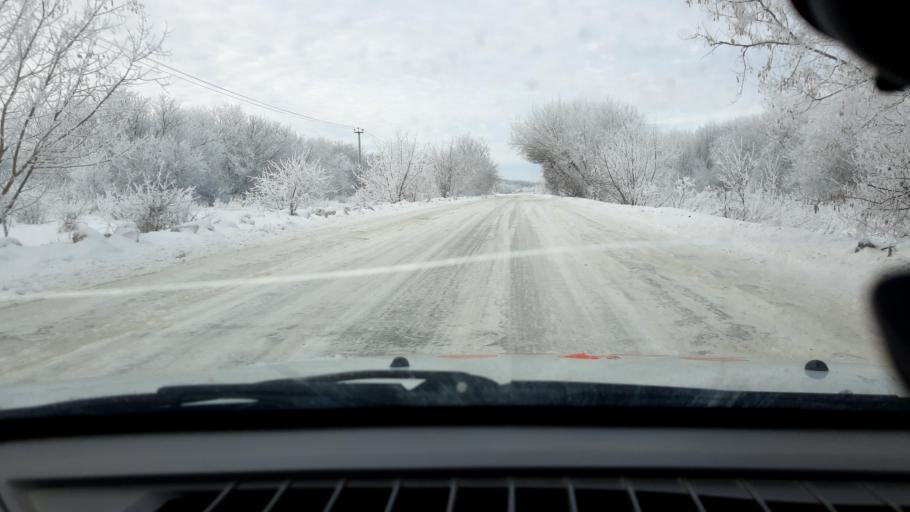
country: RU
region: Nizjnij Novgorod
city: Bogorodsk
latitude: 56.0674
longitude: 43.5858
